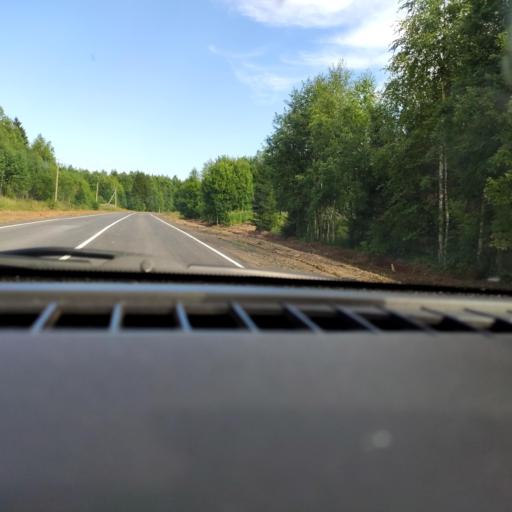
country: RU
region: Perm
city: Polazna
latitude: 58.3381
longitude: 56.1808
